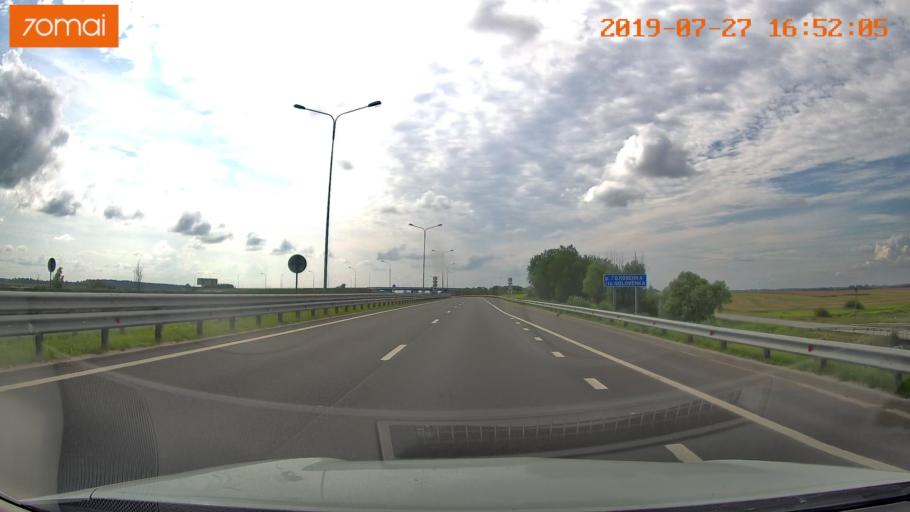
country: RU
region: Kaliningrad
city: Gvardeysk
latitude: 54.6839
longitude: 20.8704
